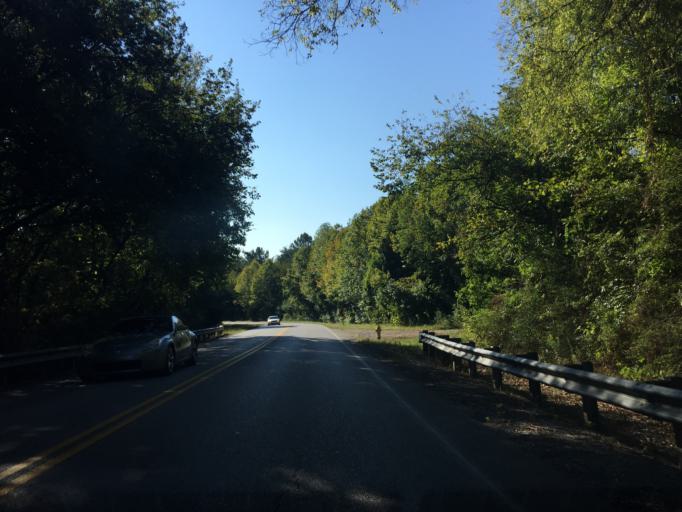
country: US
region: Tennessee
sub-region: Hamilton County
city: Harrison
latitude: 35.0854
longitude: -85.1611
